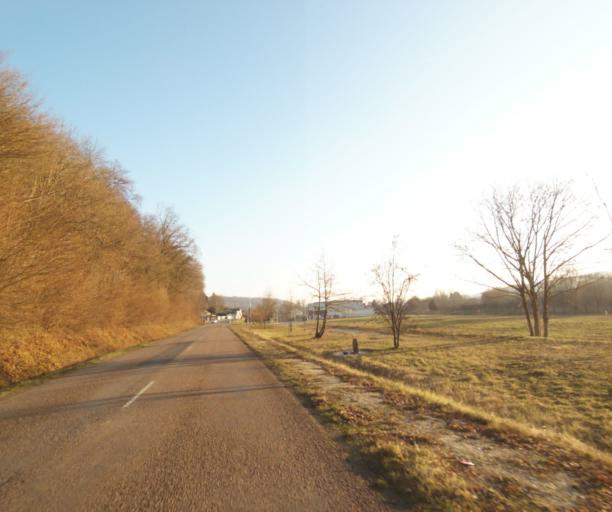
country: FR
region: Champagne-Ardenne
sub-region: Departement de la Haute-Marne
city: Chevillon
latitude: 48.5276
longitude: 5.1102
